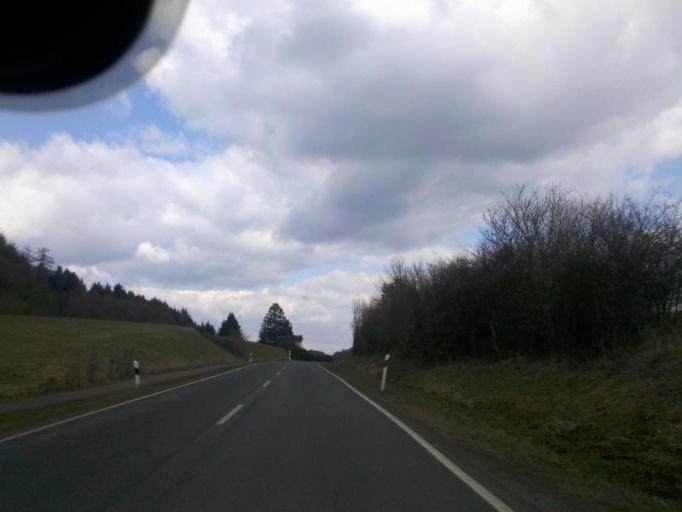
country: DE
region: Hesse
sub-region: Regierungsbezirk Giessen
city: Breidenbach
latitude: 50.8430
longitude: 8.4545
